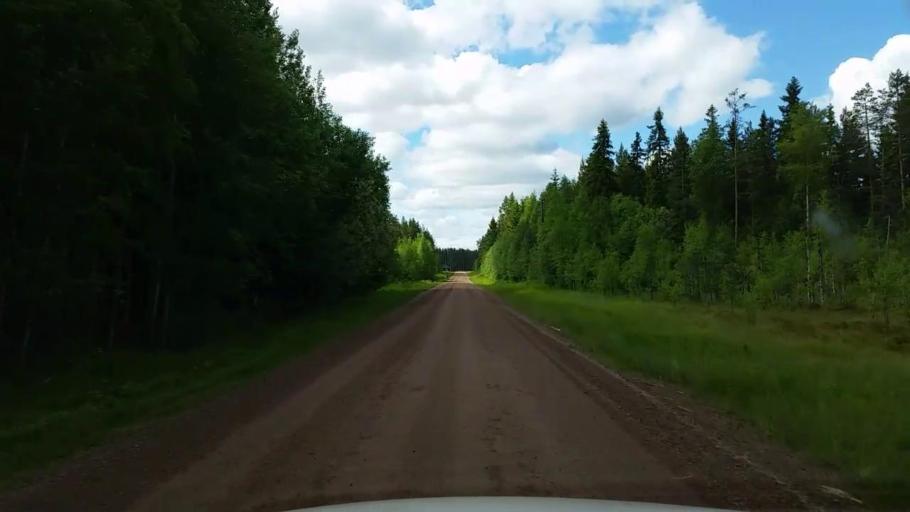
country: SE
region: Gaevleborg
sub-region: Ovanakers Kommun
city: Alfta
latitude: 61.4760
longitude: 16.0055
